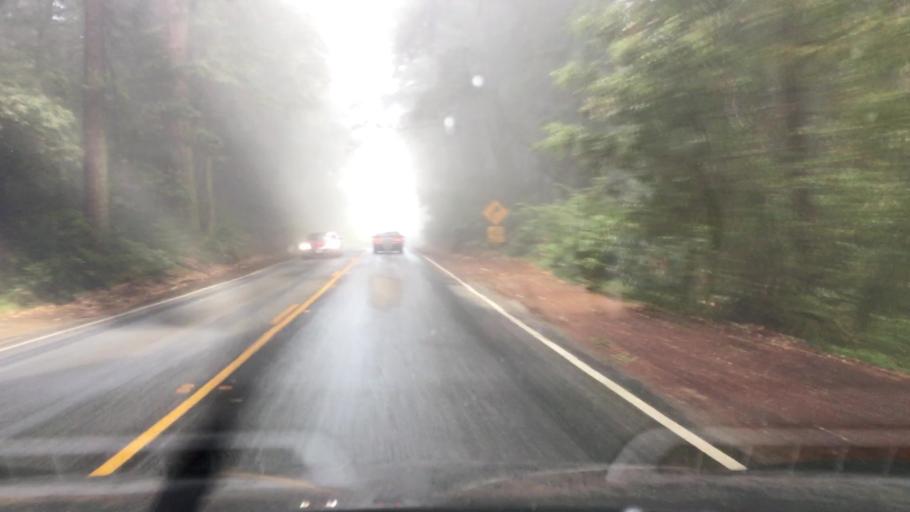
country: US
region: California
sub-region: San Mateo County
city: Emerald Lake Hills
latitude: 37.4292
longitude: -122.3124
